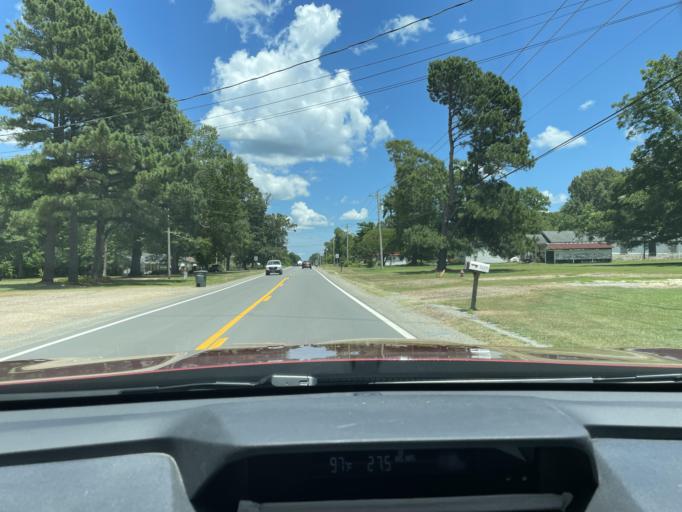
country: US
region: Arkansas
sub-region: Drew County
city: Monticello
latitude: 33.6283
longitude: -91.7648
